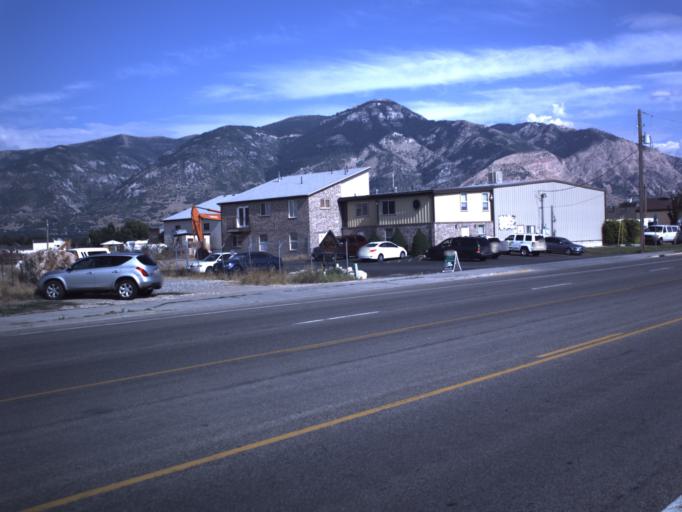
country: US
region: Utah
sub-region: Weber County
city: Pleasant View
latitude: 41.3033
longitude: -112.0025
